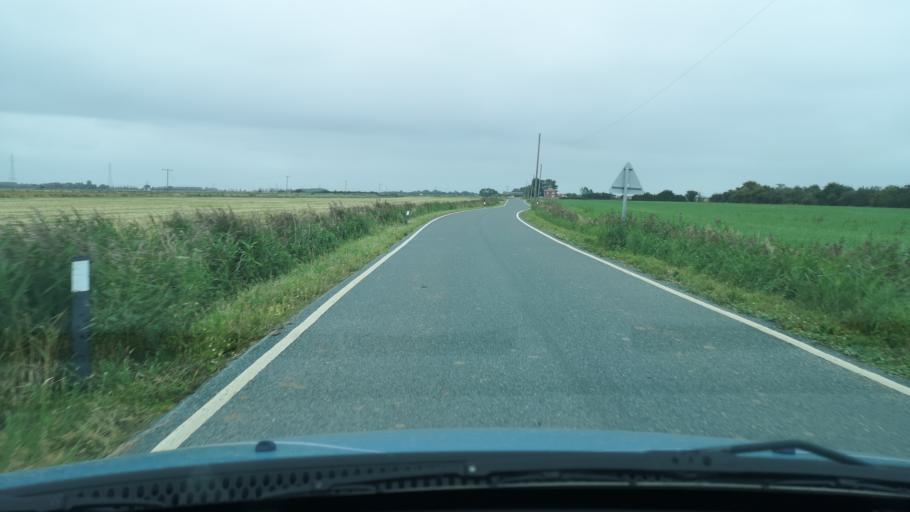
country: GB
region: England
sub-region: North Lincolnshire
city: Burton upon Stather
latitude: 53.6826
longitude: -0.7223
